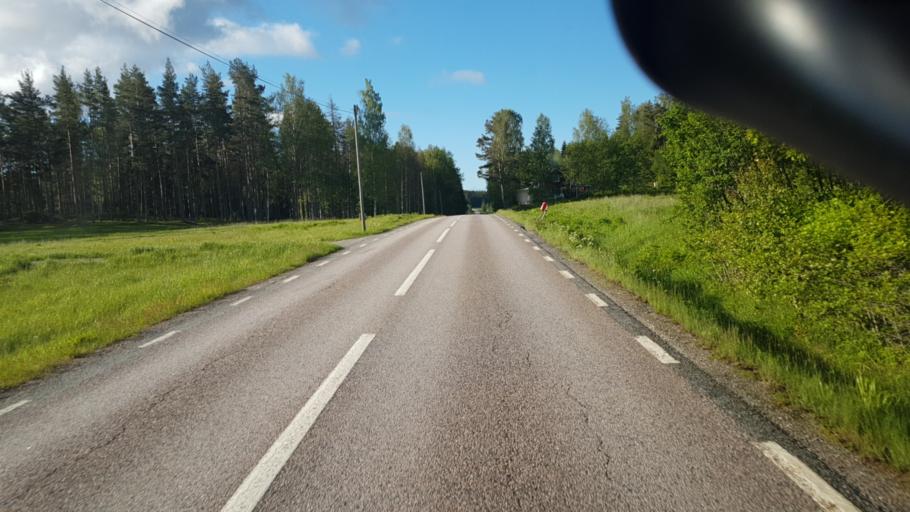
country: SE
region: Vaermland
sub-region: Arvika Kommun
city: Arvika
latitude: 59.6004
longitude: 12.5359
